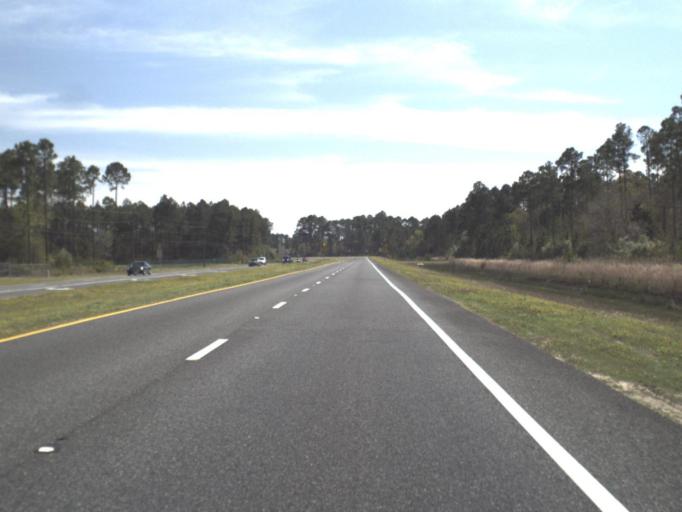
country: US
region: Florida
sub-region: Bay County
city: Lynn Haven
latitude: 30.3292
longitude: -85.6605
